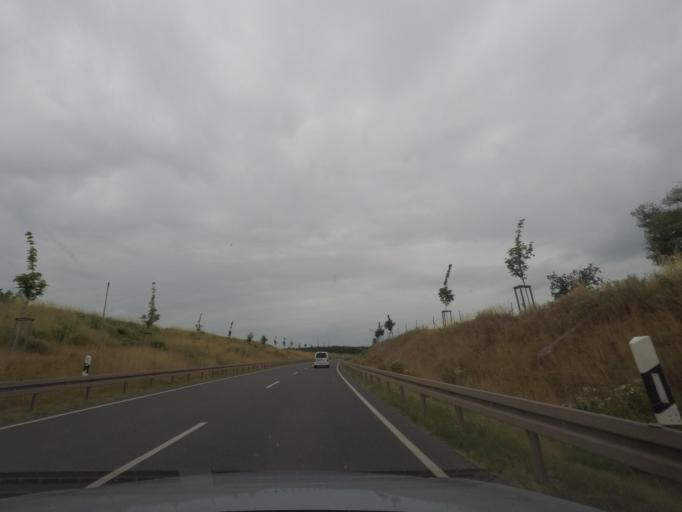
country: DE
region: Saxony-Anhalt
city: Suplingen
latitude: 52.2484
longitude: 11.3551
